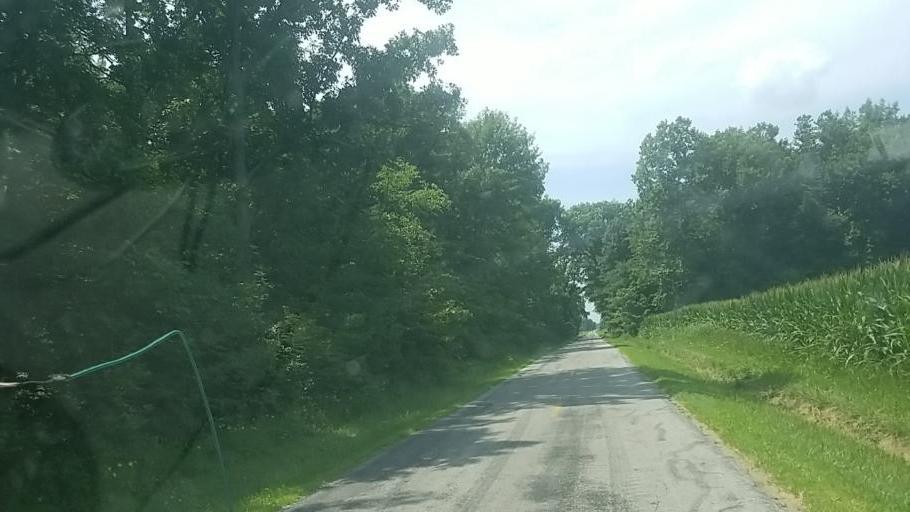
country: US
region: Ohio
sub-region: Union County
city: Richwood
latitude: 40.6074
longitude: -83.3322
